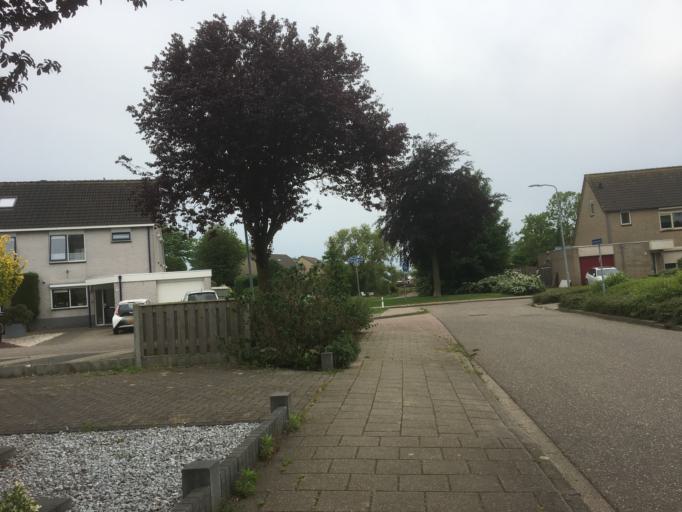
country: NL
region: Gelderland
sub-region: Gemeente Duiven
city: Duiven
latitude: 51.9409
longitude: 6.0139
